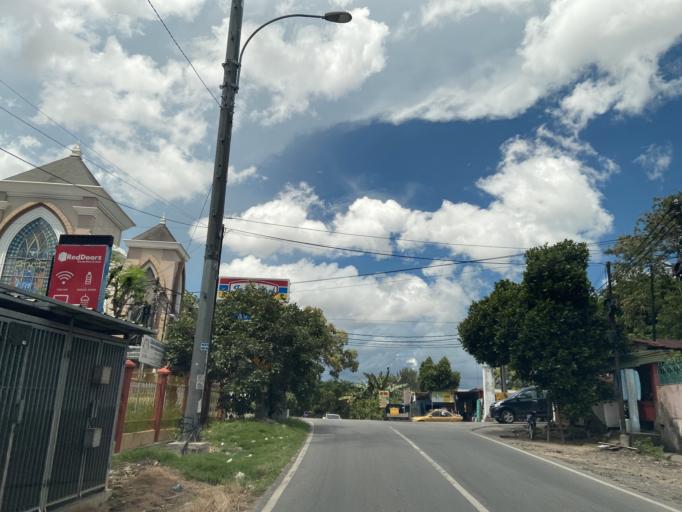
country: SG
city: Singapore
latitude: 1.1353
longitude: 104.0145
